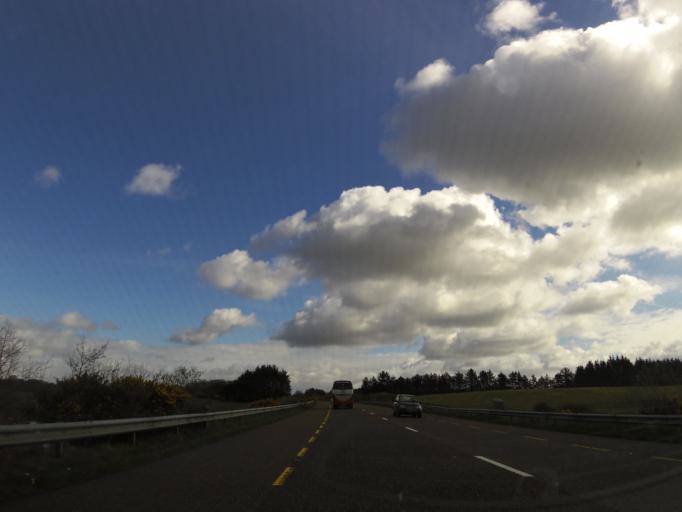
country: IE
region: Connaught
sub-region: Maigh Eo
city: Kiltamagh
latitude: 53.8107
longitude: -8.9019
